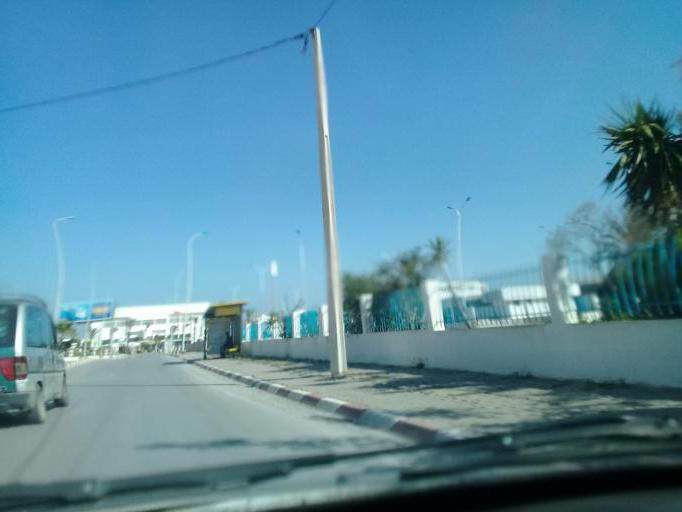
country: TN
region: Tunis
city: La Goulette
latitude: 36.8135
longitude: 10.3028
